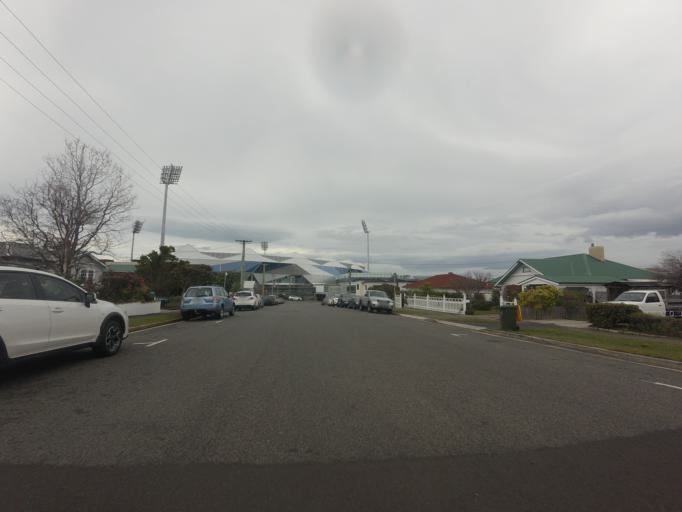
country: AU
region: Tasmania
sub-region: Clarence
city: Bellerive
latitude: -42.8770
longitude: 147.3710
